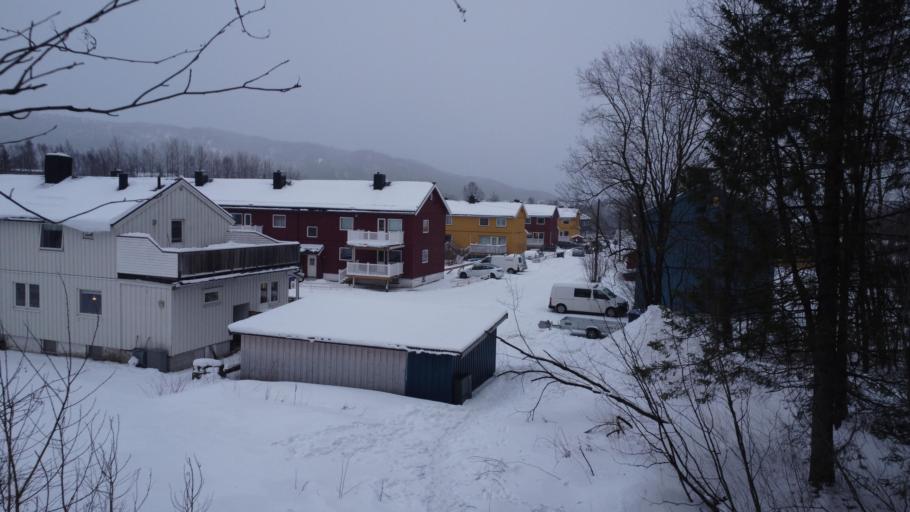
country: NO
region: Nordland
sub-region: Rana
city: Mo i Rana
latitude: 66.3152
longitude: 14.1608
